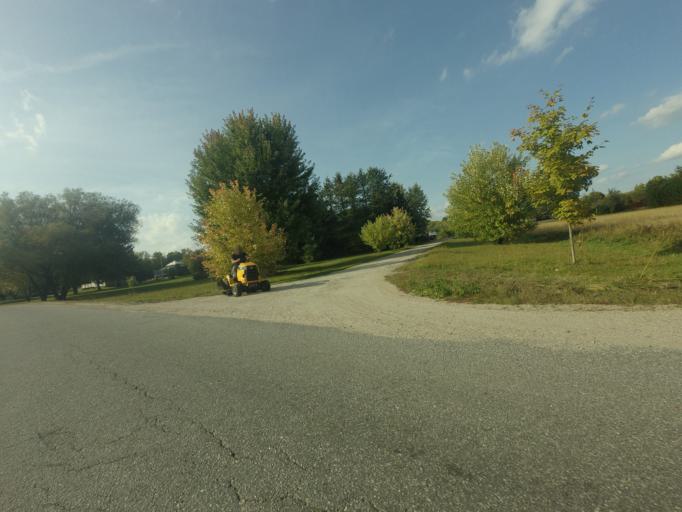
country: CA
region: Quebec
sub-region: Outaouais
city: Maniwaki
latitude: 46.3657
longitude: -75.9961
